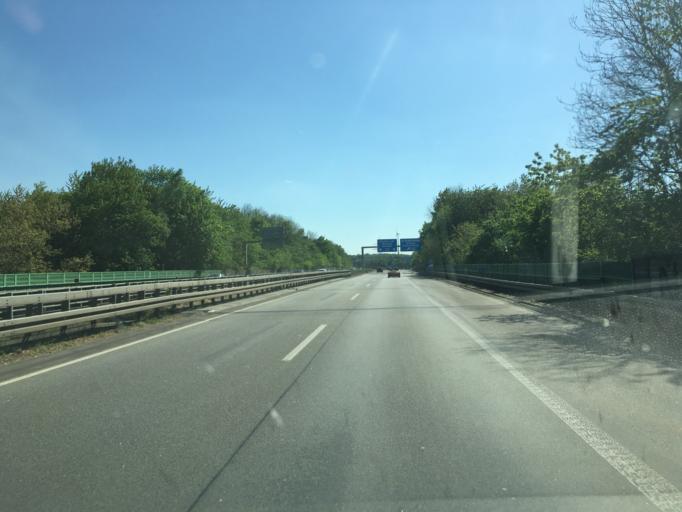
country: DE
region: North Rhine-Westphalia
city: Castrop-Rauxel
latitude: 51.5680
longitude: 7.3612
